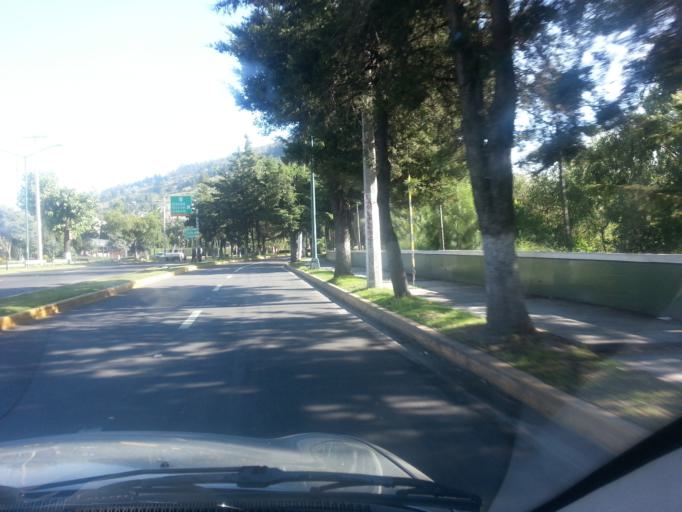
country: MX
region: Mexico
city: San Buenaventura
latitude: 19.2859
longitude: -99.6804
